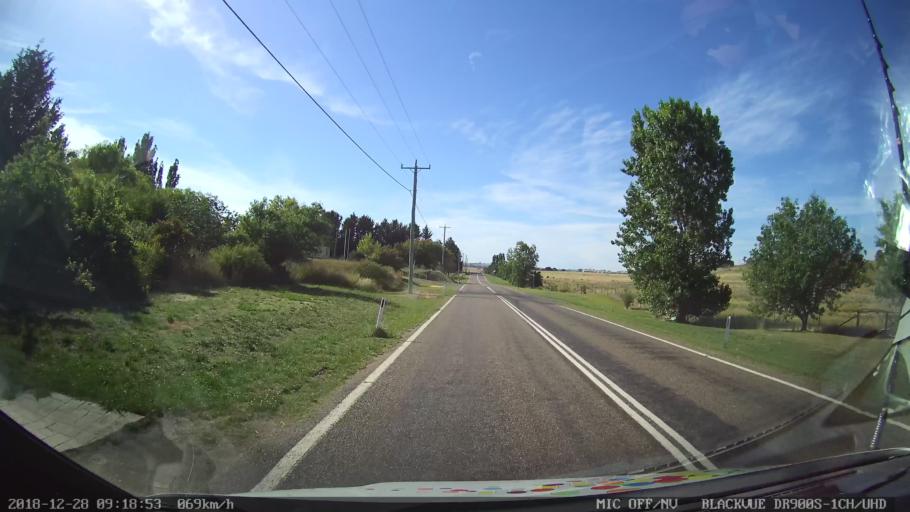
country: AU
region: New South Wales
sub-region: Upper Lachlan Shire
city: Crookwell
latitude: -34.3306
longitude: 149.3661
